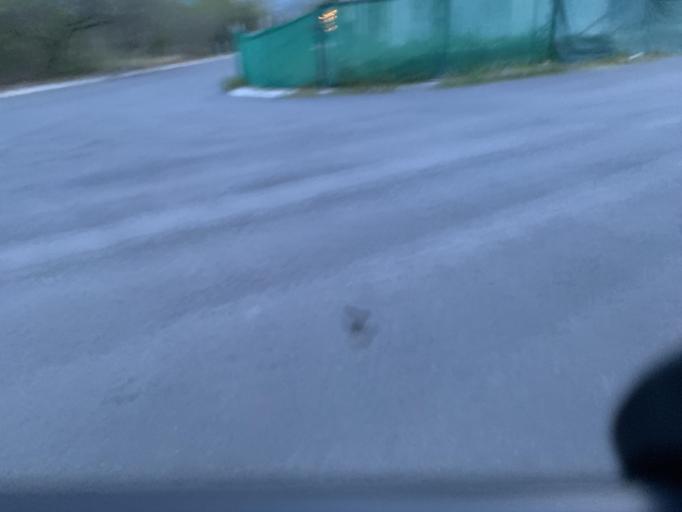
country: MX
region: Nuevo Leon
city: Santiago
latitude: 25.5049
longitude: -100.1849
